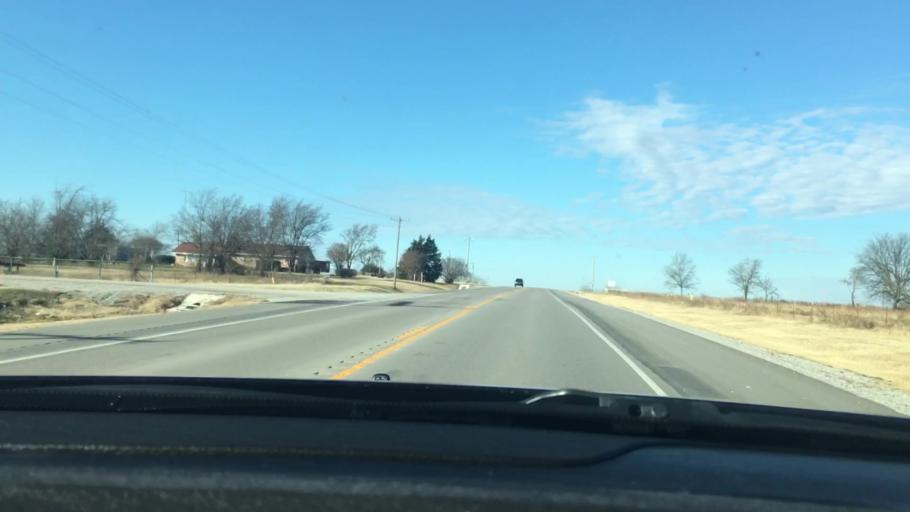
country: US
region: Oklahoma
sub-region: Love County
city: Marietta
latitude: 33.9404
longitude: -97.1846
